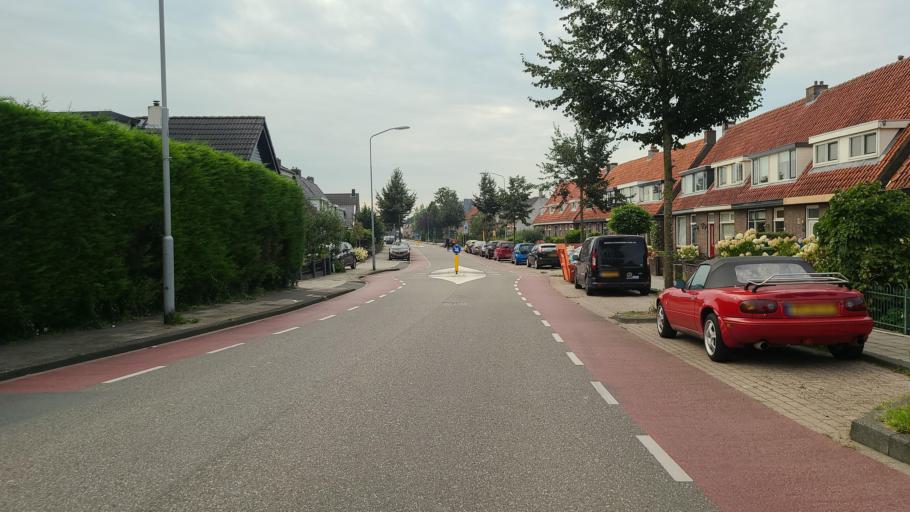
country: NL
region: Gelderland
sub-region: Gemeente Tiel
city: Tiel
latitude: 51.8934
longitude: 5.4306
